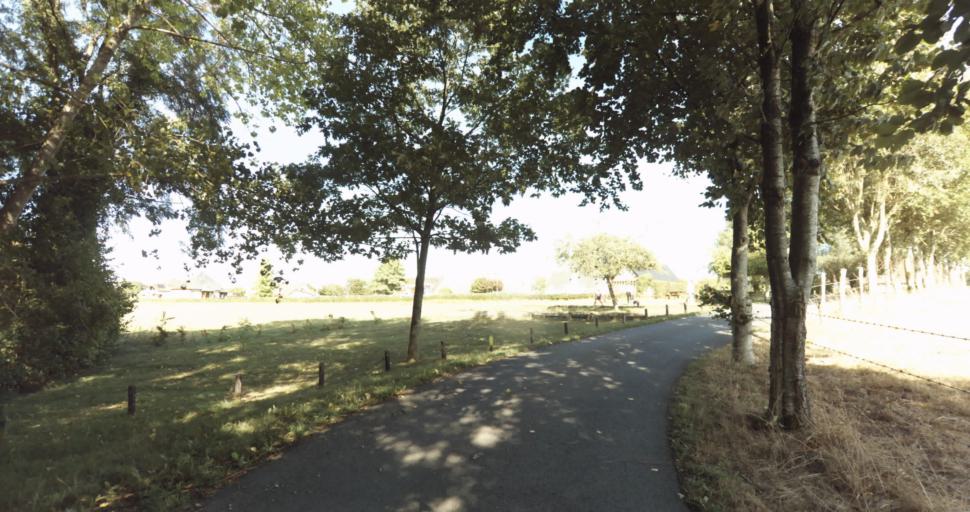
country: FR
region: Lower Normandy
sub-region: Departement de l'Orne
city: Vimoutiers
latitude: 48.9215
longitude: 0.1398
